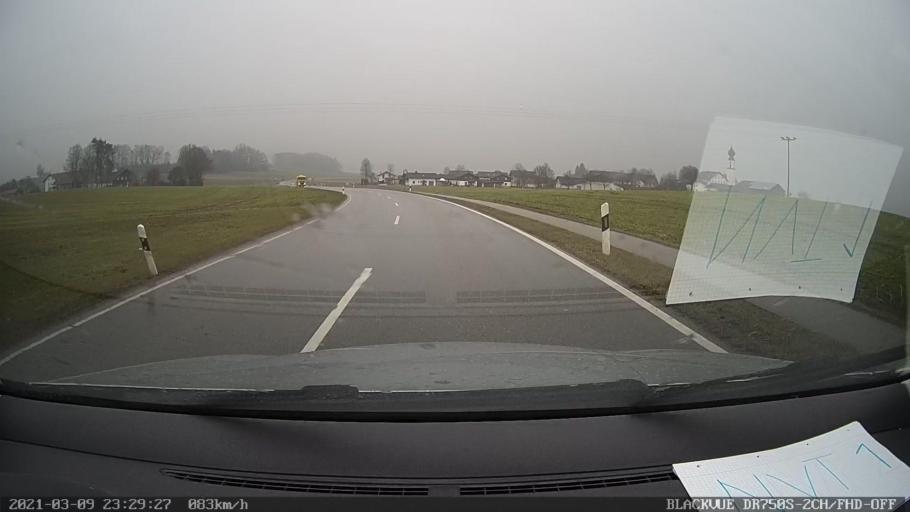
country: DE
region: Bavaria
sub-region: Upper Bavaria
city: Schonstett
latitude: 47.9859
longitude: 12.2501
